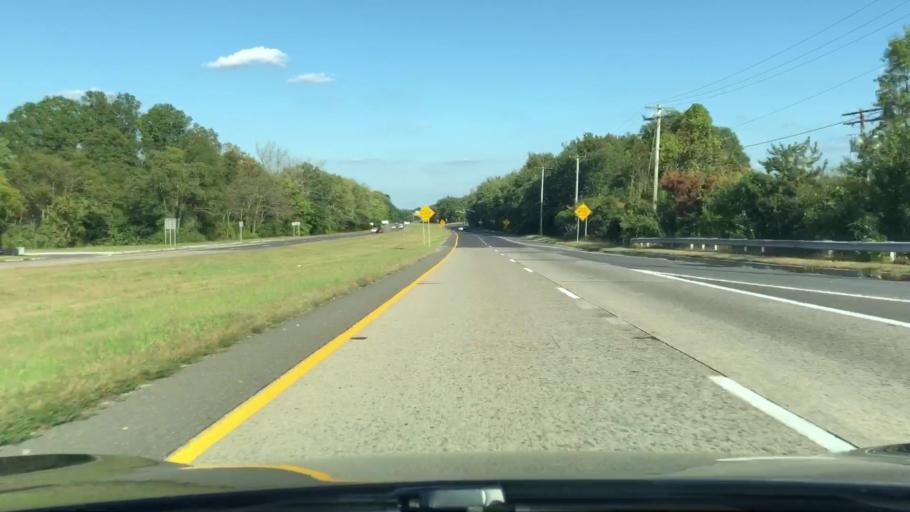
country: US
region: New Jersey
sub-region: Gloucester County
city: Gibbstown
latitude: 39.8031
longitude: -75.3217
